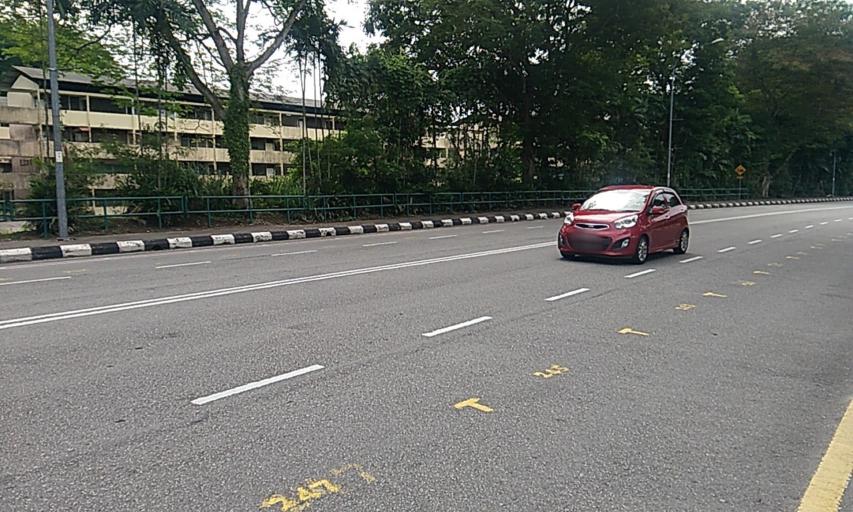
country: MY
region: Perak
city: Ipoh
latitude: 4.6010
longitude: 101.0812
